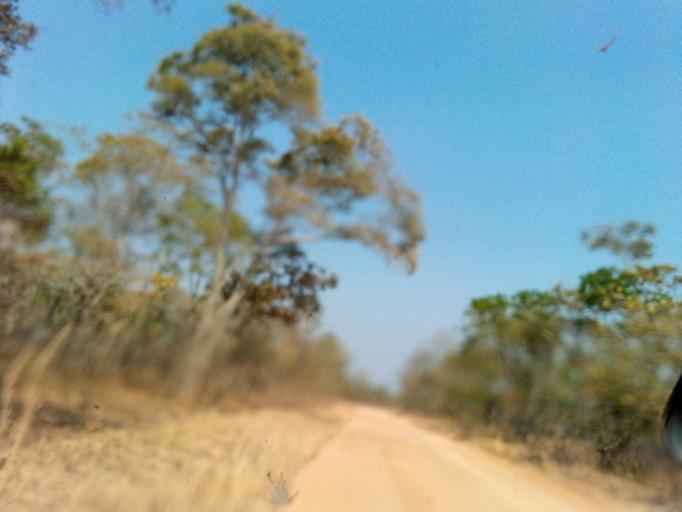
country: ZM
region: Northern
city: Mpika
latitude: -12.2416
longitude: 30.8250
